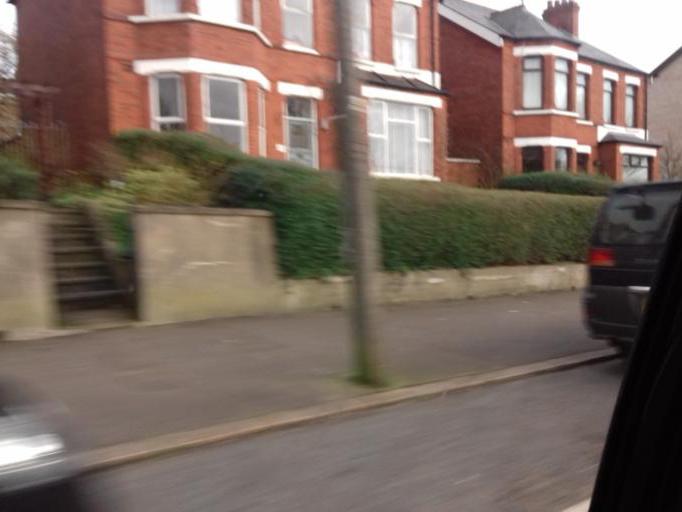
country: GB
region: Northern Ireland
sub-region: City of Belfast
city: Belfast
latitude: 54.6274
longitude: -5.9437
